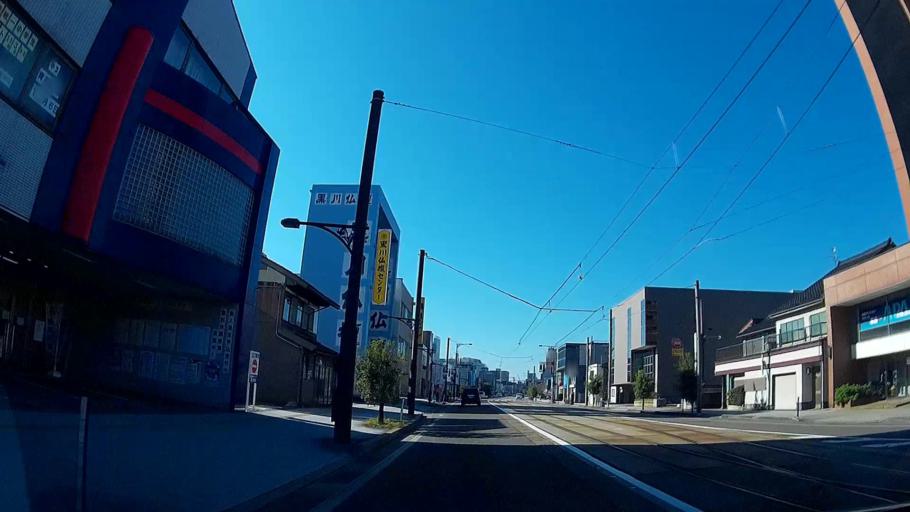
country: JP
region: Toyama
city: Takaoka
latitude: 36.7499
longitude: 137.0180
